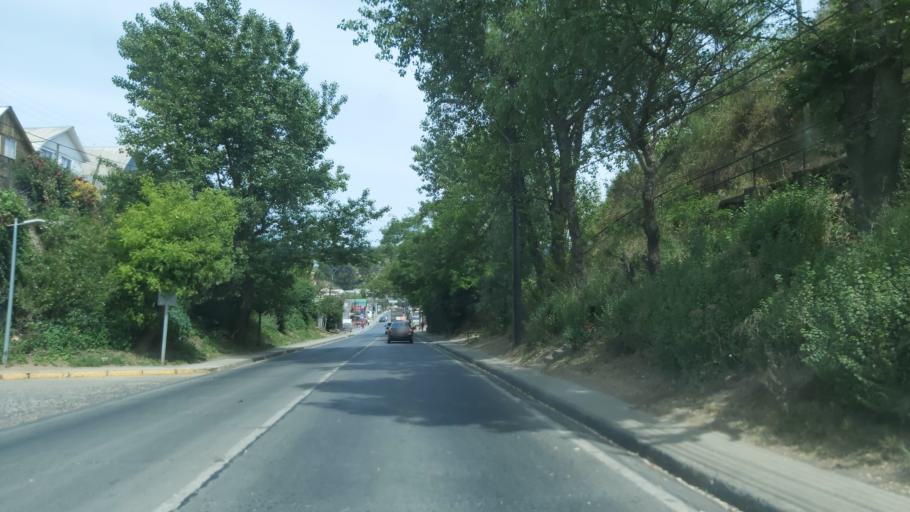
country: CL
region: Maule
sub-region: Provincia de Talca
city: Constitucion
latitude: -35.3299
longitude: -72.4189
